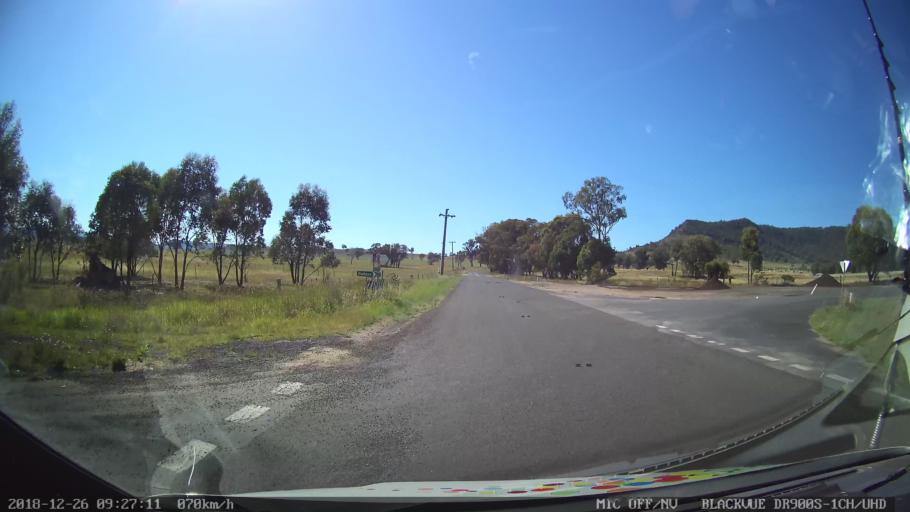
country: AU
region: New South Wales
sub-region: Mid-Western Regional
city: Kandos
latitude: -32.8335
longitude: 150.0152
